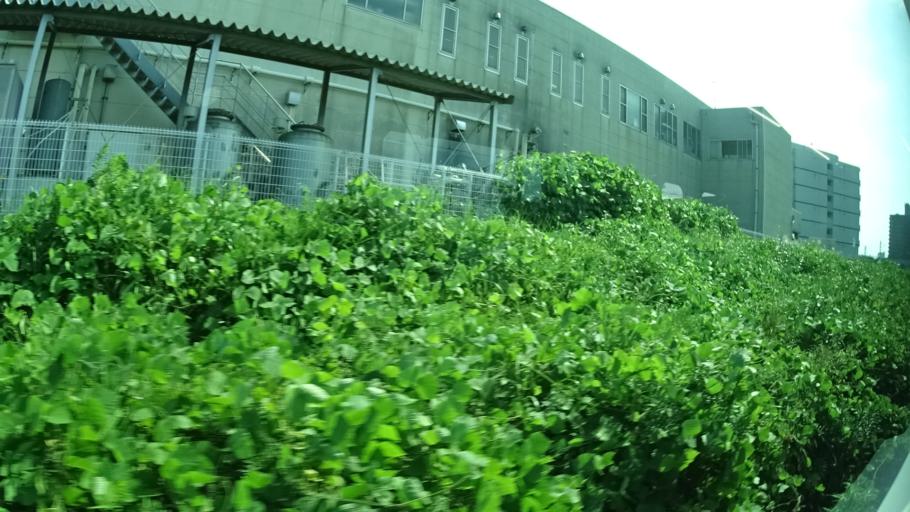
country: JP
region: Miyagi
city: Sendai-shi
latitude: 38.2697
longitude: 140.8994
